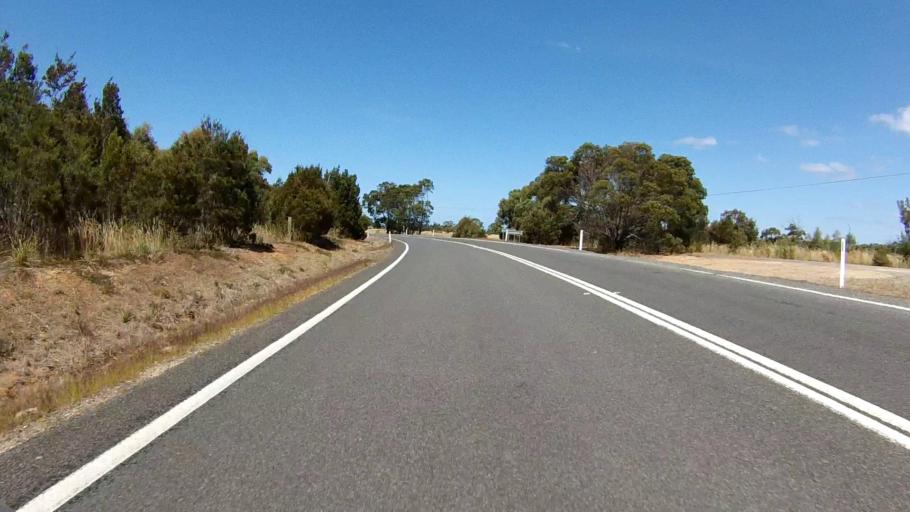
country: AU
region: Tasmania
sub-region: Break O'Day
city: St Helens
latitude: -42.0513
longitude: 148.0531
